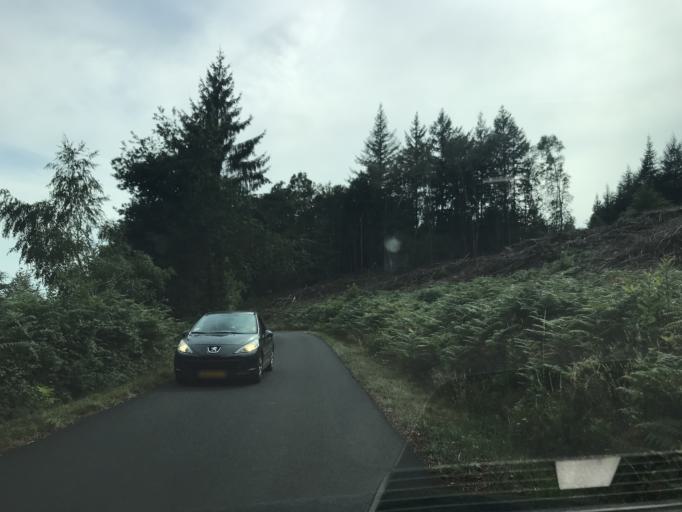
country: FR
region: Limousin
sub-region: Departement de la Correze
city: Neuvic
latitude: 45.3772
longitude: 2.2504
